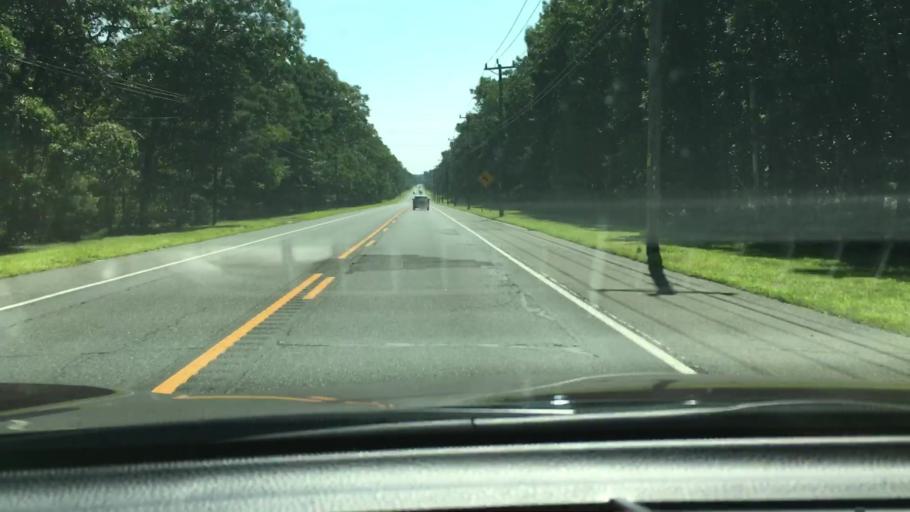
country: US
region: New Jersey
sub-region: Cumberland County
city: Laurel Lake
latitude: 39.3803
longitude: -74.9683
